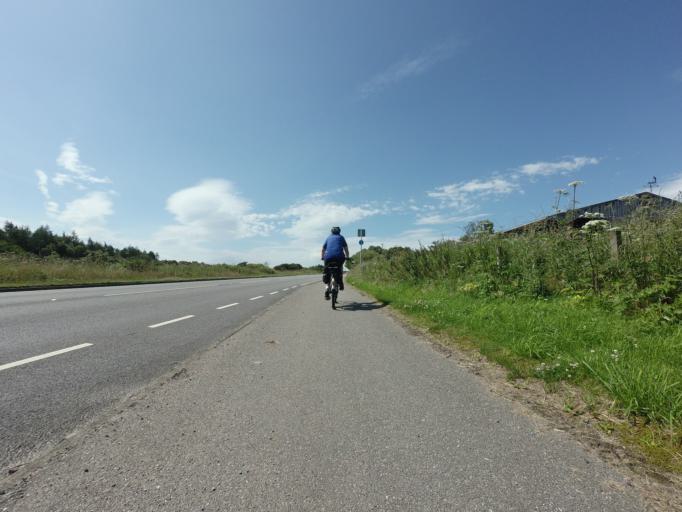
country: GB
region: Scotland
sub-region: Highland
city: Conon Bridge
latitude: 57.5394
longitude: -4.3523
